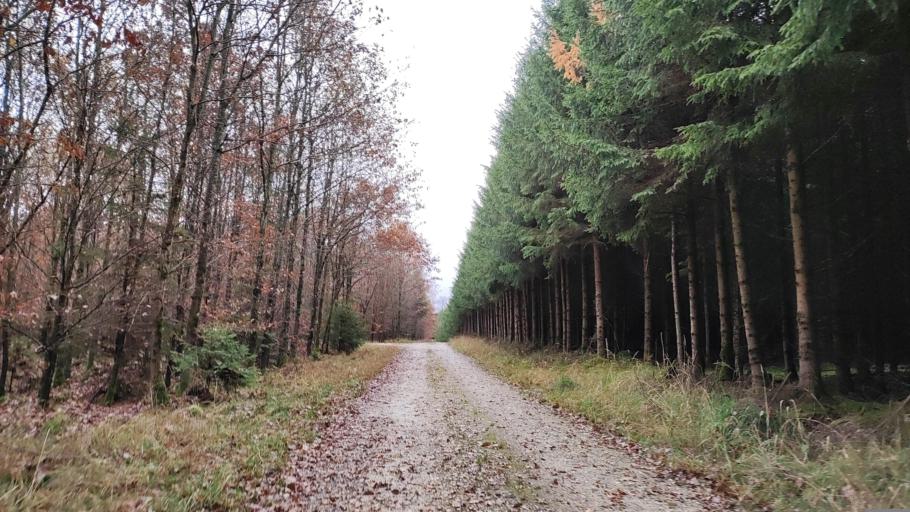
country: DE
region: Bavaria
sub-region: Swabia
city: Burtenbach
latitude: 48.3602
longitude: 10.5168
